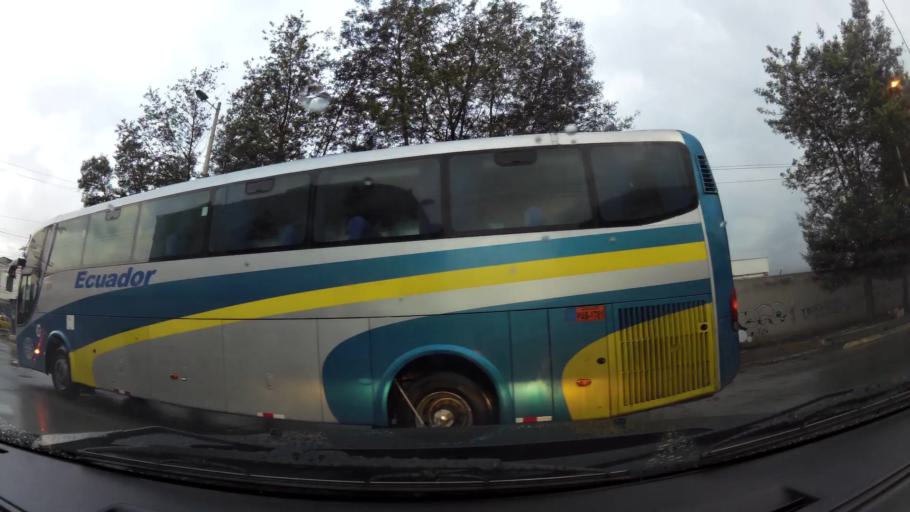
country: EC
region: Pichincha
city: Quito
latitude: -0.3041
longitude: -78.5433
